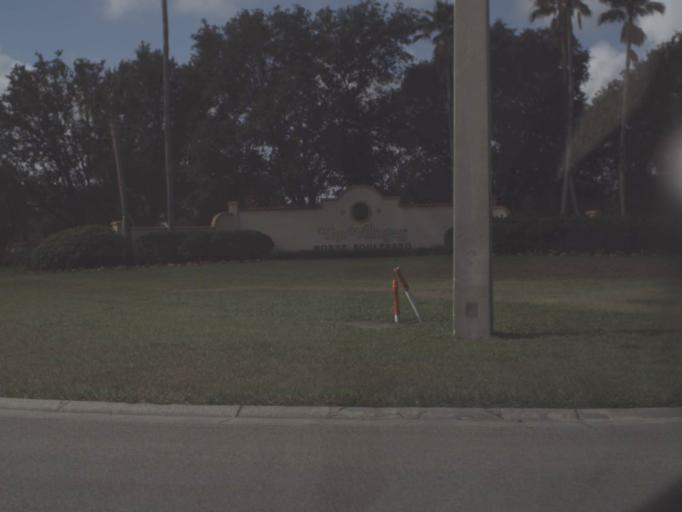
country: US
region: Florida
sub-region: Sumter County
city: The Villages
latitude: 28.9489
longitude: -81.9542
